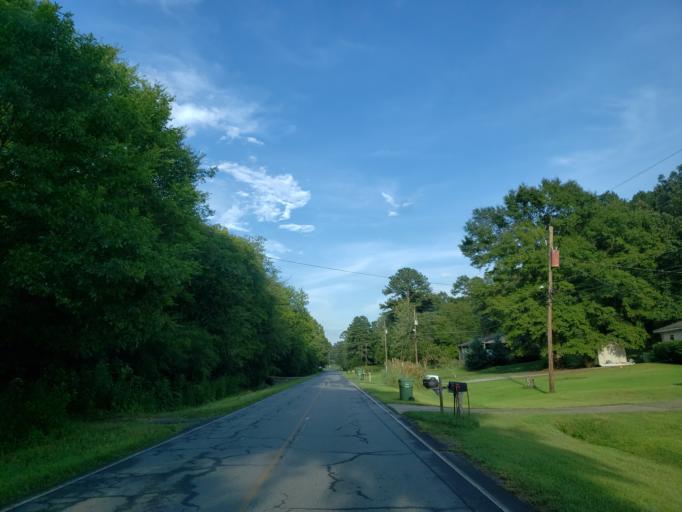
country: US
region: Georgia
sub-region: Bartow County
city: Euharlee
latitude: 34.2280
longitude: -84.9657
